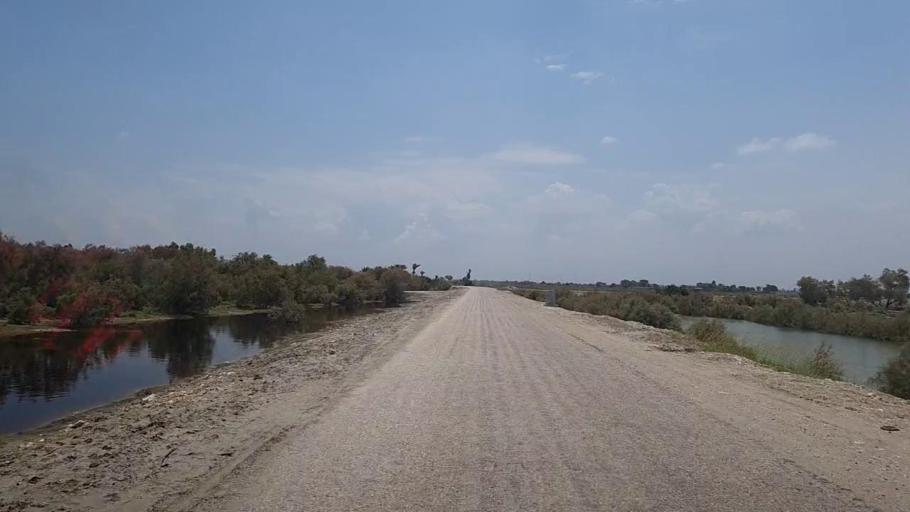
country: PK
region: Sindh
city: Kandhkot
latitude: 28.2821
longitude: 69.1697
